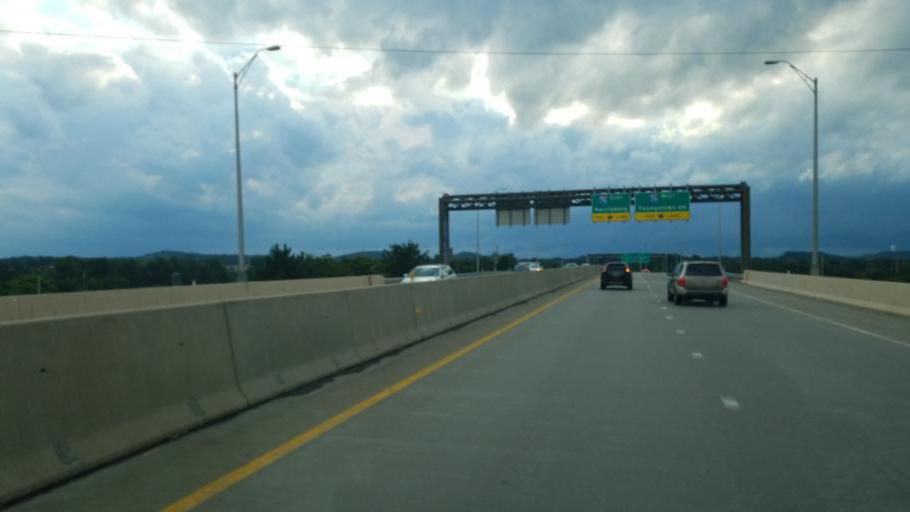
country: US
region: Pennsylvania
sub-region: Butler County
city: Cranberry Township
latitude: 40.6782
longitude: -80.0996
